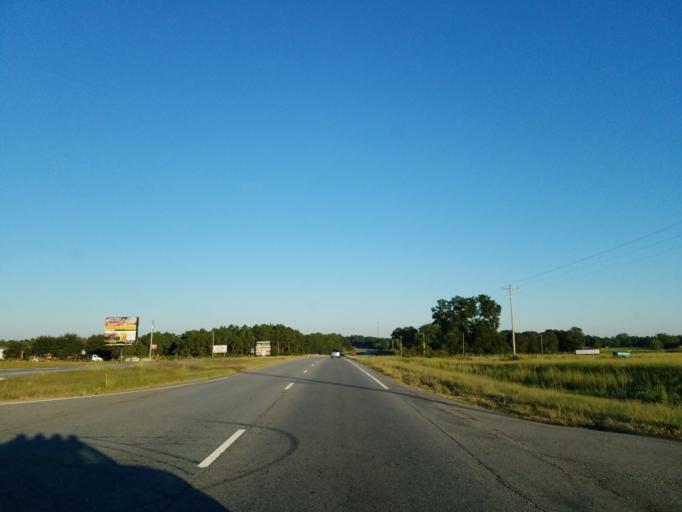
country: US
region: Georgia
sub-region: Tift County
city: Omega
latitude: 31.4780
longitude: -83.6784
